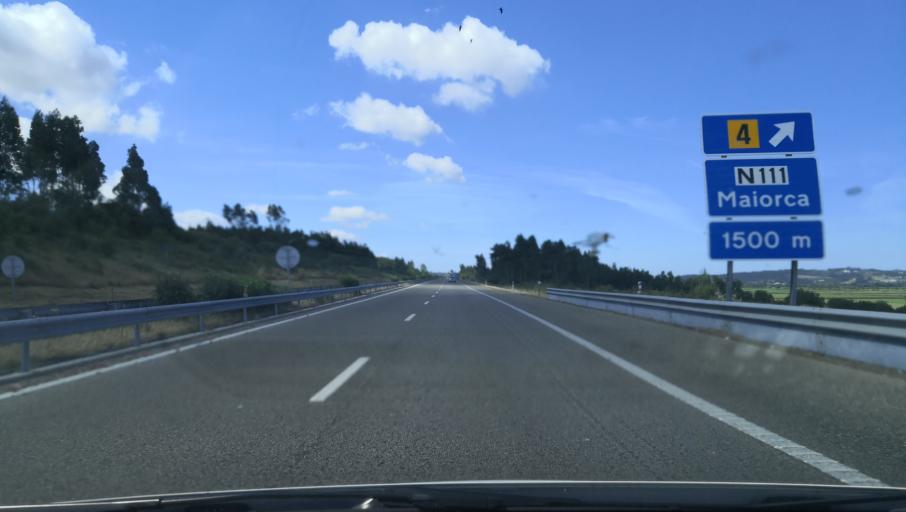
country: PT
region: Coimbra
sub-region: Montemor-O-Velho
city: Montemor-o-Velho
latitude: 40.1872
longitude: -8.7009
